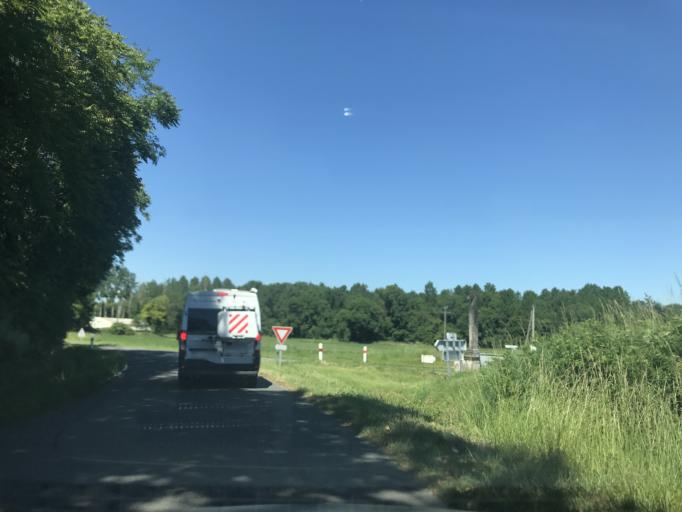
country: FR
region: Poitou-Charentes
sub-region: Departement de la Charente-Maritime
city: Mortagne-sur-Gironde
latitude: 45.4273
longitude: -0.7075
